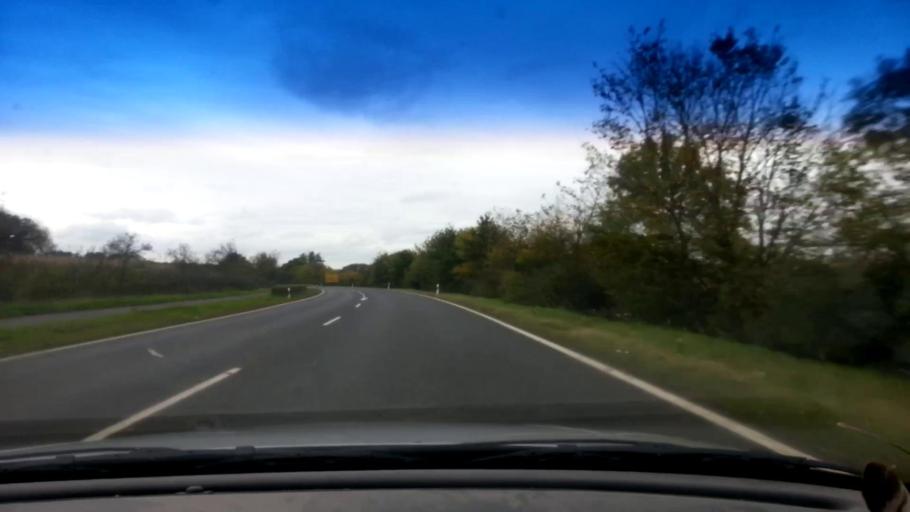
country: DE
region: Bavaria
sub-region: Upper Franconia
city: Reckendorf
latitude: 50.0014
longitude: 10.8393
